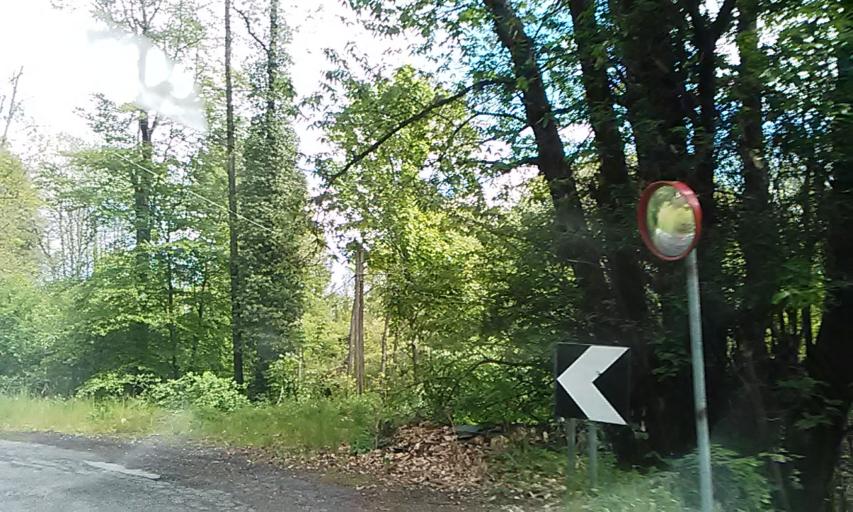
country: IT
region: Piedmont
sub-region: Provincia di Vercelli
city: Cellio
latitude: 45.7586
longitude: 8.3065
